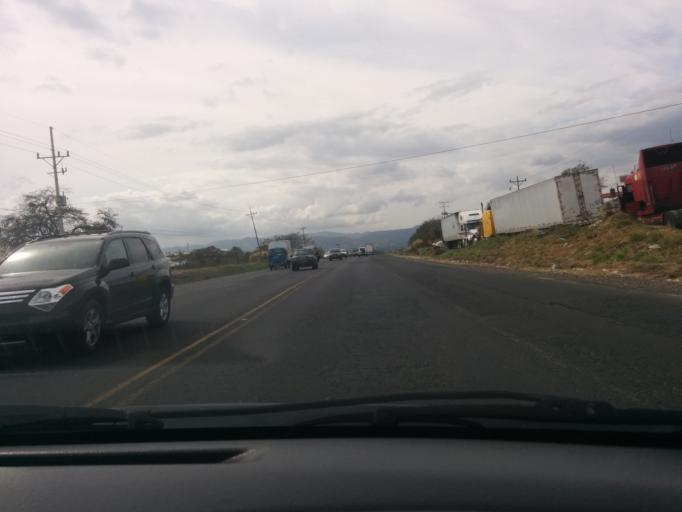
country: CR
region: Alajuela
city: Carrillos
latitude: 9.9977
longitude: -84.2741
